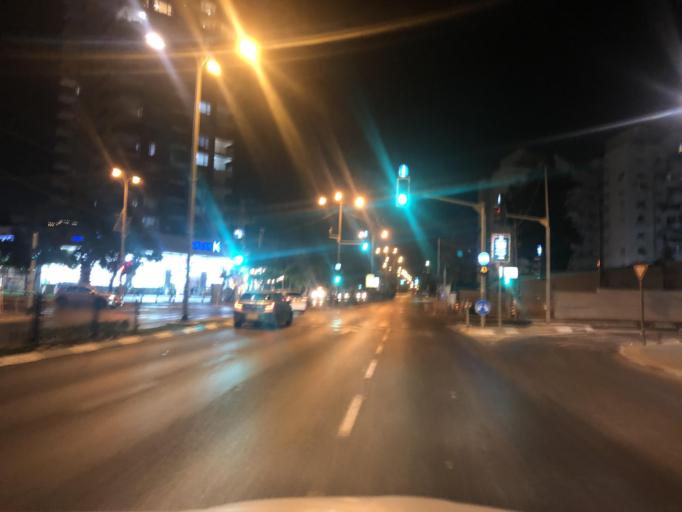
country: IL
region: Tel Aviv
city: Azor
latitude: 32.0470
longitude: 34.7985
